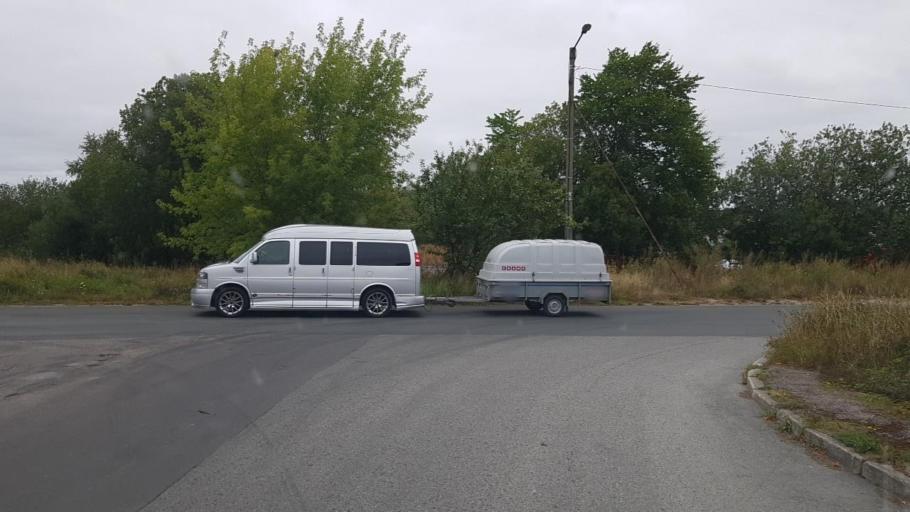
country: EE
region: Harju
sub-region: Tallinna linn
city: Tallinn
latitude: 59.4222
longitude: 24.6820
